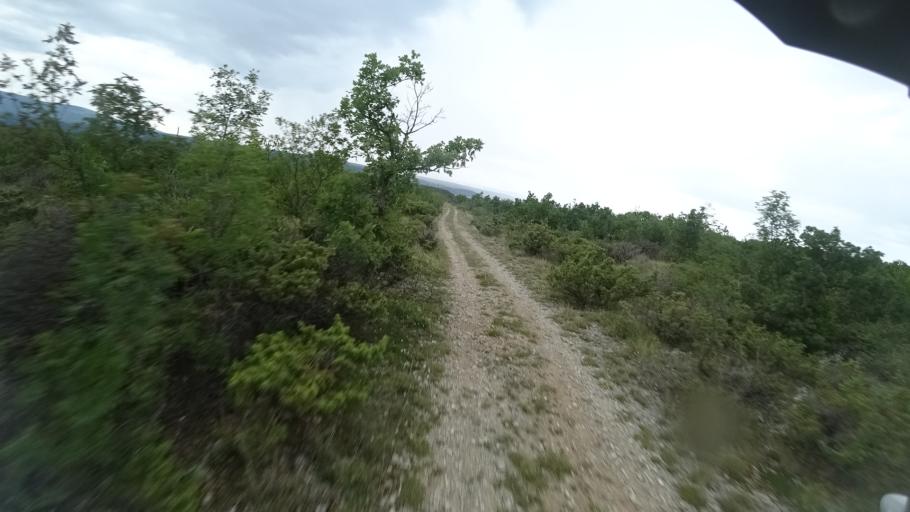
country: HR
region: Sibensko-Kniniska
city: Knin
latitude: 44.0327
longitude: 16.2467
